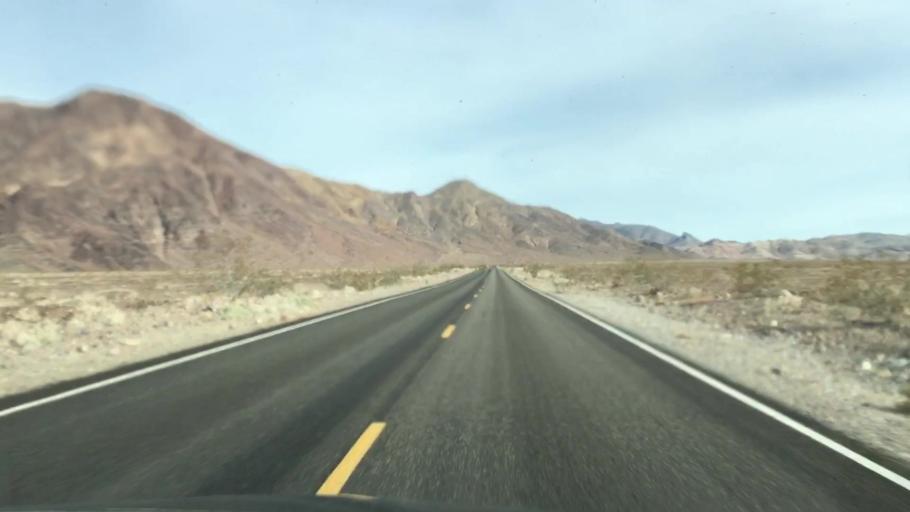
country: US
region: Nevada
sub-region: Nye County
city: Beatty
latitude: 36.6901
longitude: -117.0037
